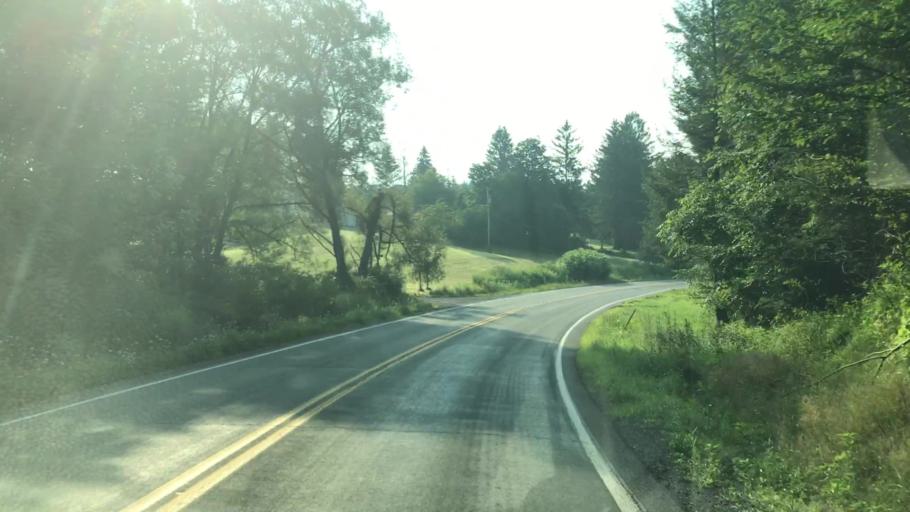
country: US
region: Pennsylvania
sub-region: Lackawanna County
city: Dalton
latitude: 41.5975
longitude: -75.6648
